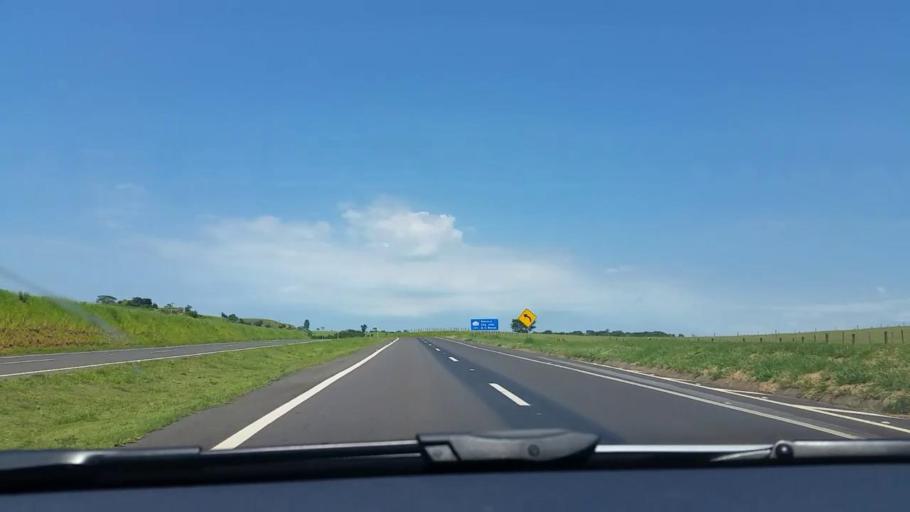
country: BR
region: Sao Paulo
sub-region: Bauru
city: Bauru
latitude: -22.4265
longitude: -49.1289
